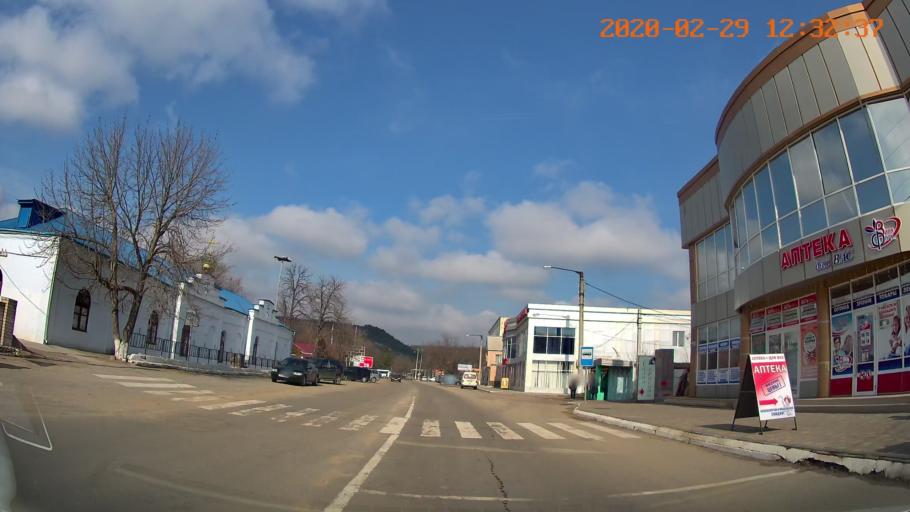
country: MD
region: Telenesti
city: Camenca
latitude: 48.0296
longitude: 28.7031
